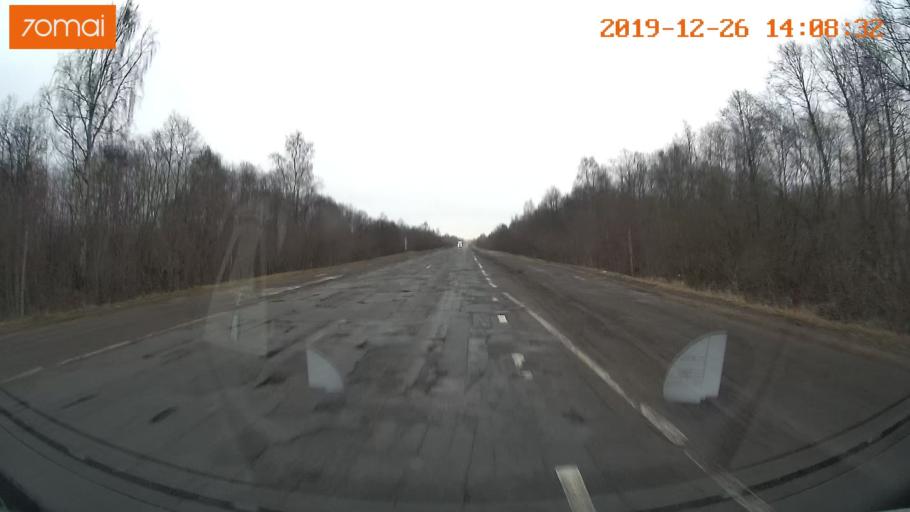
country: RU
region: Jaroslavl
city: Poshekhon'ye
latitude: 58.5087
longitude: 38.9146
